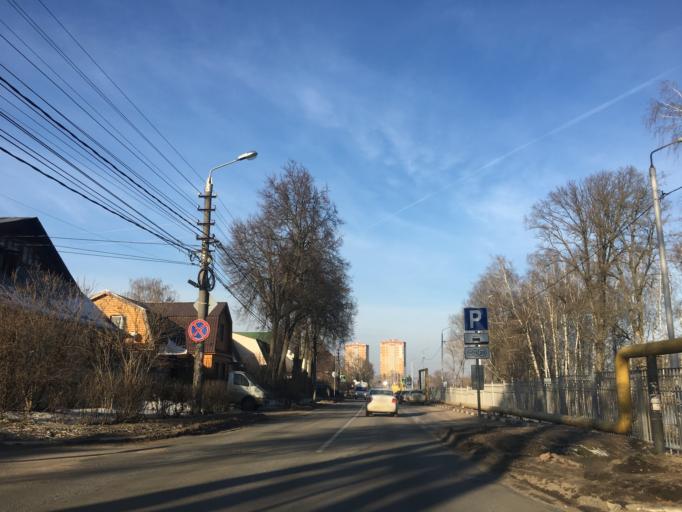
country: RU
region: Tula
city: Tula
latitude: 54.1828
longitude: 37.5768
